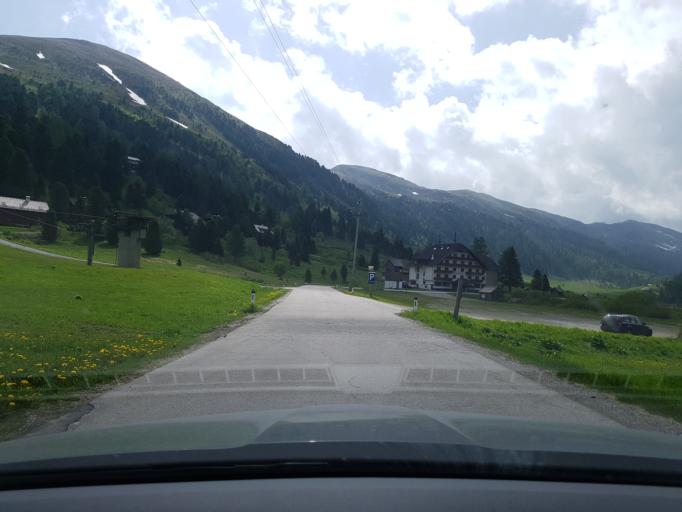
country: AT
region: Salzburg
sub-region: Politischer Bezirk Tamsweg
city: Thomatal
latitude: 46.9841
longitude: 13.7742
